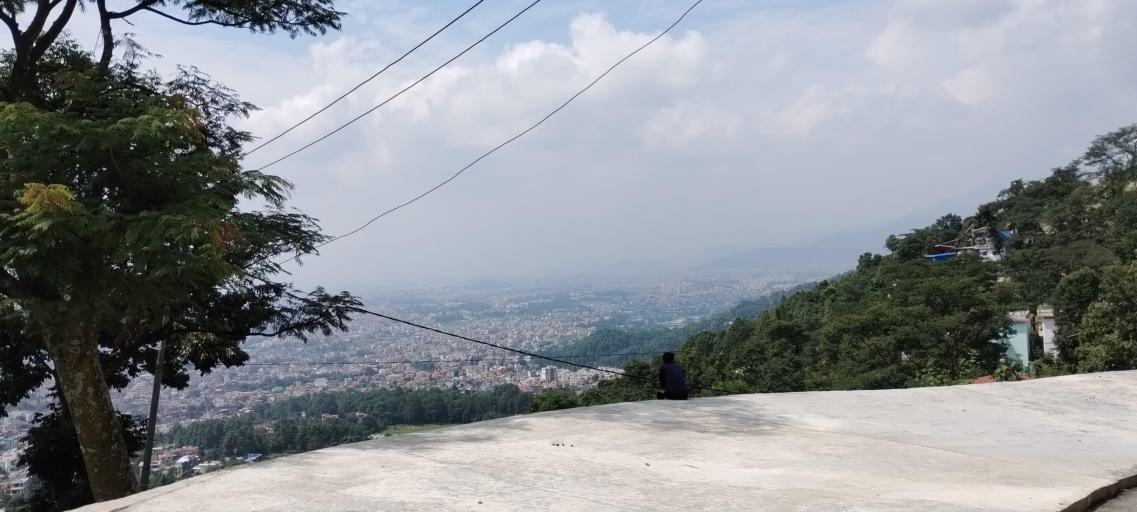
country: NP
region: Central Region
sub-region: Bagmati Zone
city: Kathmandu
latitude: 27.7900
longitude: 85.3653
